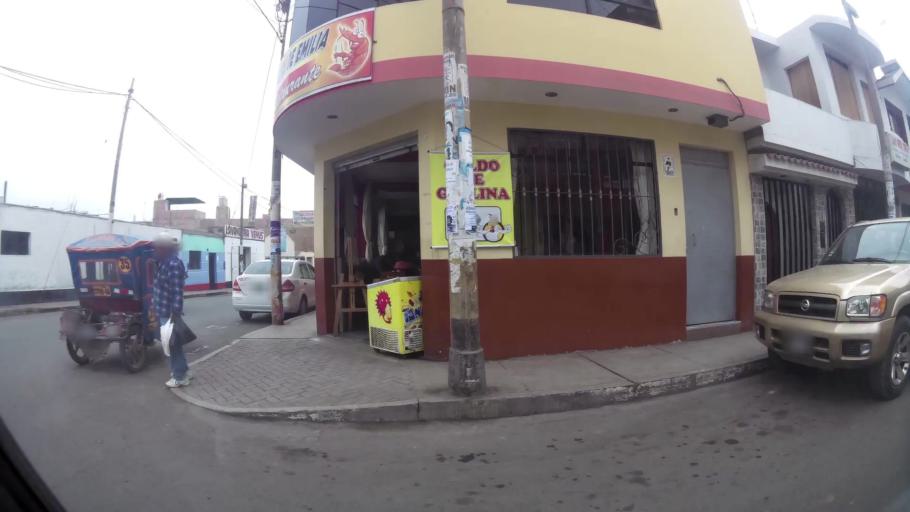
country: PE
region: Lima
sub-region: Provincia de Huaral
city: Huaral
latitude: -11.4970
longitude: -77.2068
